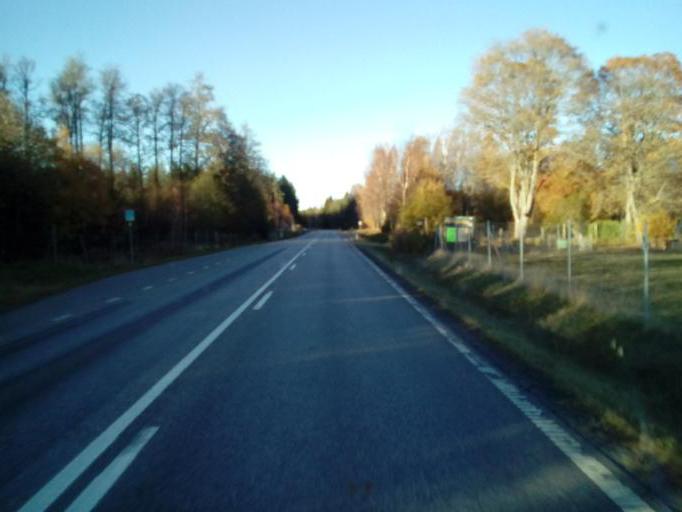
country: SE
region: OErebro
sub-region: Hallsbergs Kommun
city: Palsboda
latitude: 58.9515
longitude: 15.4162
